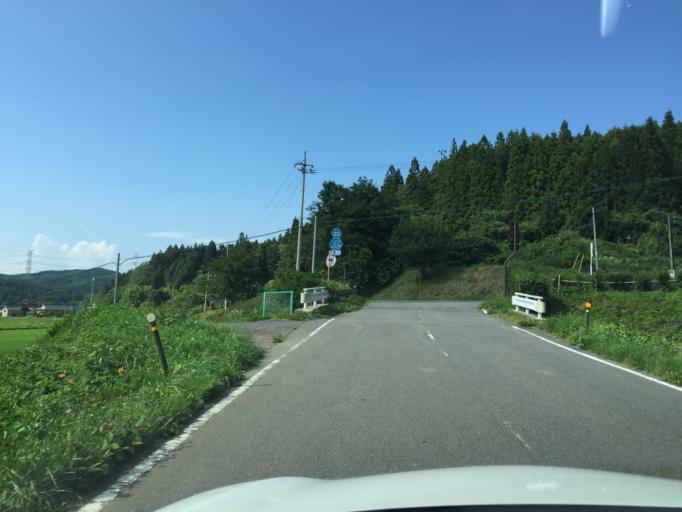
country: JP
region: Fukushima
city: Ishikawa
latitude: 37.1799
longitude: 140.6241
